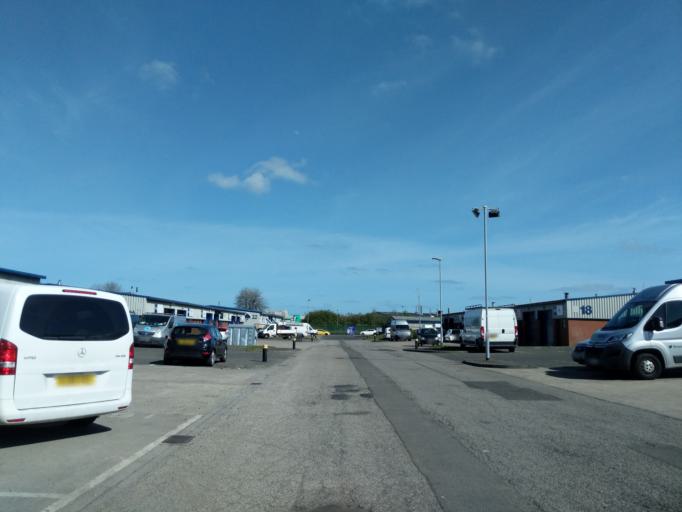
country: GB
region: England
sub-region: Northumberland
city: Cramlington
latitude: 55.0971
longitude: -1.6090
